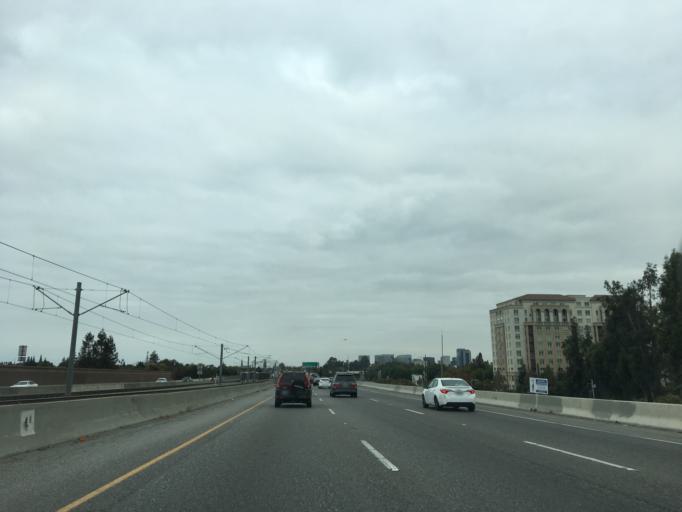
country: US
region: California
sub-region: Santa Clara County
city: San Jose
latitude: 37.3087
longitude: -121.8821
